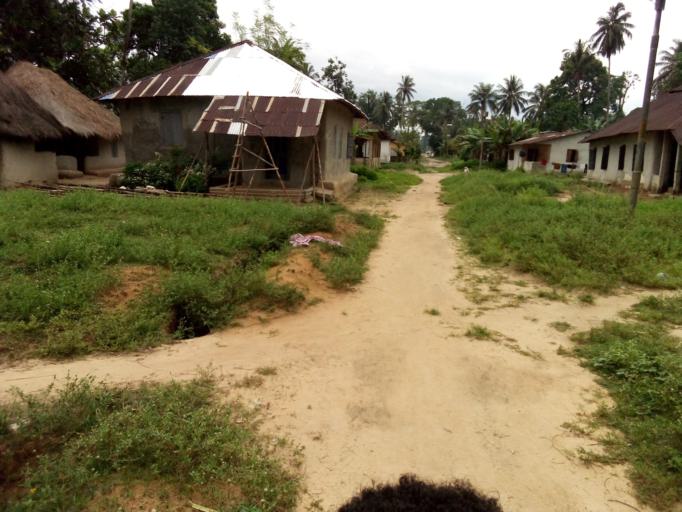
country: SL
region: Southern Province
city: Bonthe
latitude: 7.5224
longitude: -12.5046
